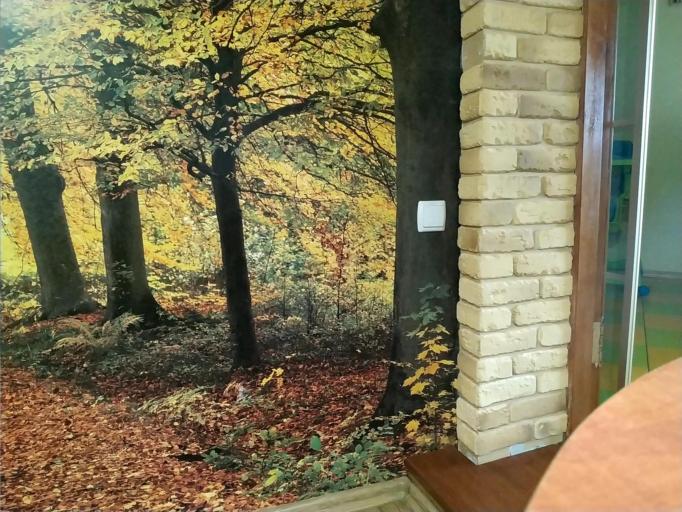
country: RU
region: Smolensk
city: Dorogobuzh
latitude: 54.9031
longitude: 33.3235
